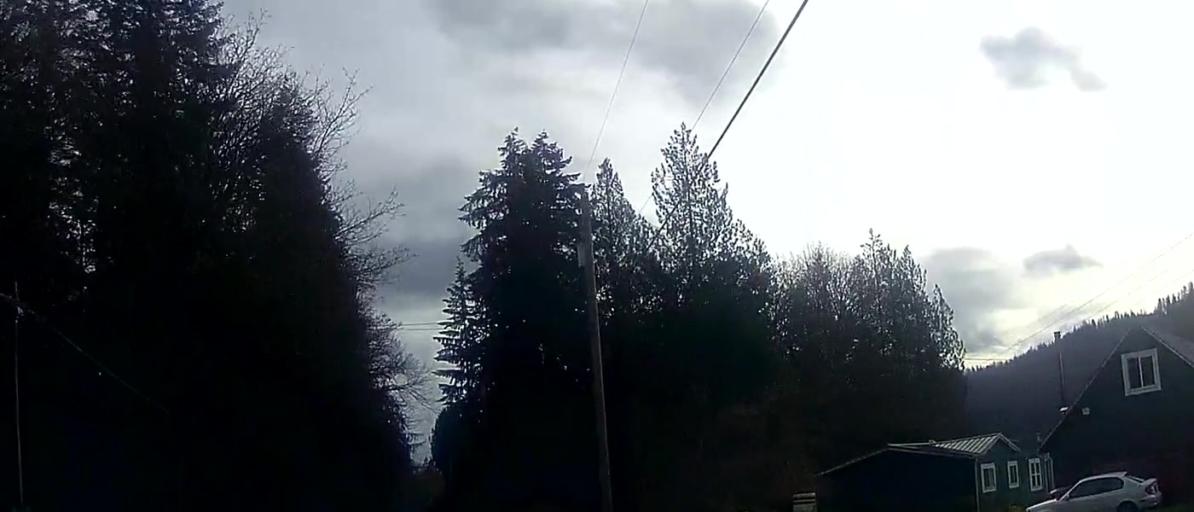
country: US
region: Washington
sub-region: Skagit County
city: Sedro-Woolley
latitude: 48.5644
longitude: -122.2958
